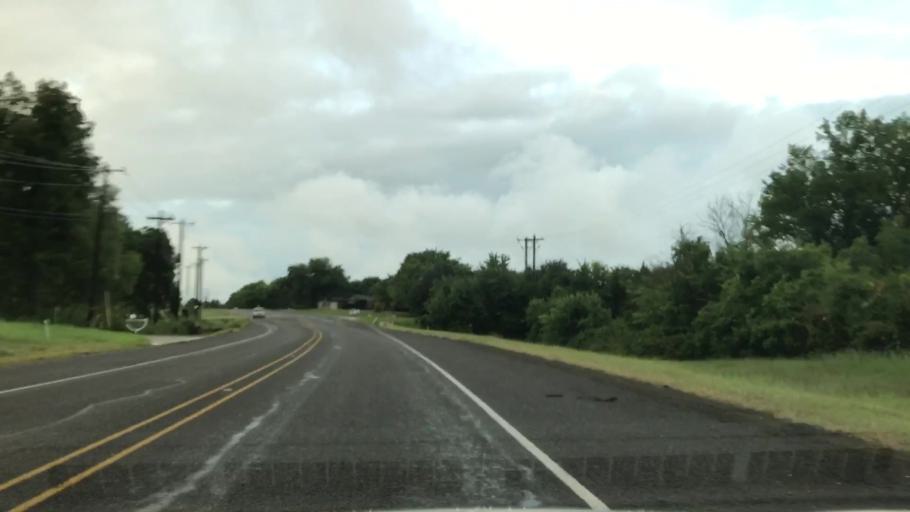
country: US
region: Texas
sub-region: Rockwall County
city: Rockwall
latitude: 32.9745
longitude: -96.4668
